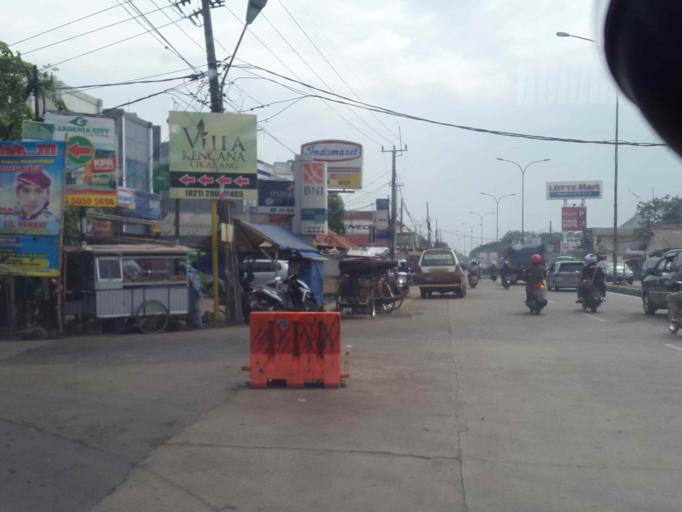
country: ID
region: West Java
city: Cikarang
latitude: -6.2575
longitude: 107.1561
